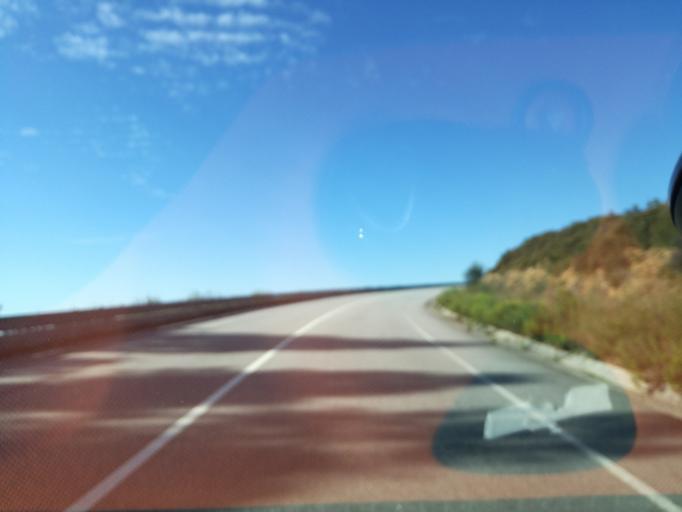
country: PT
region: Porto
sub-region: Pacos de Ferreira
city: Seroa
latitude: 41.2679
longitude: -8.4420
